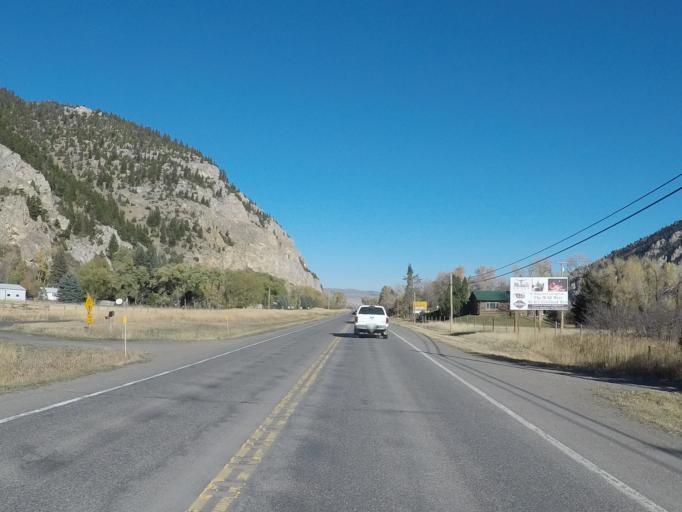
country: US
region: Montana
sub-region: Park County
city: Livingston
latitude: 45.6037
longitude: -110.5743
